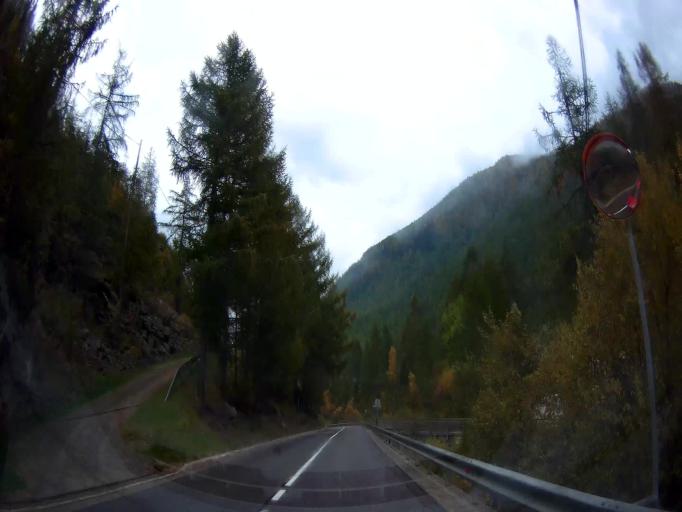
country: IT
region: Trentino-Alto Adige
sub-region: Bolzano
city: Senales
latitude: 46.7160
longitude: 10.8725
